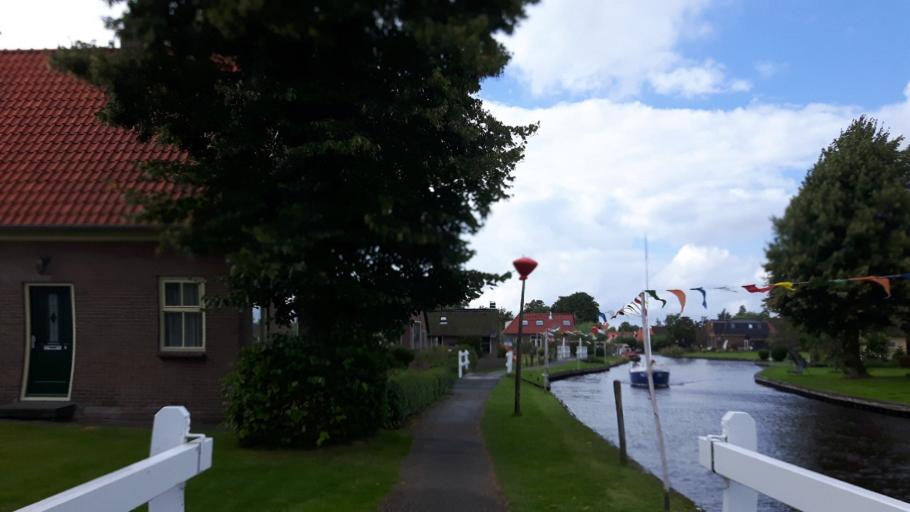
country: NL
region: Overijssel
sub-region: Gemeente Steenwijkerland
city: Blokzijl
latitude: 52.7738
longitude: 5.9599
